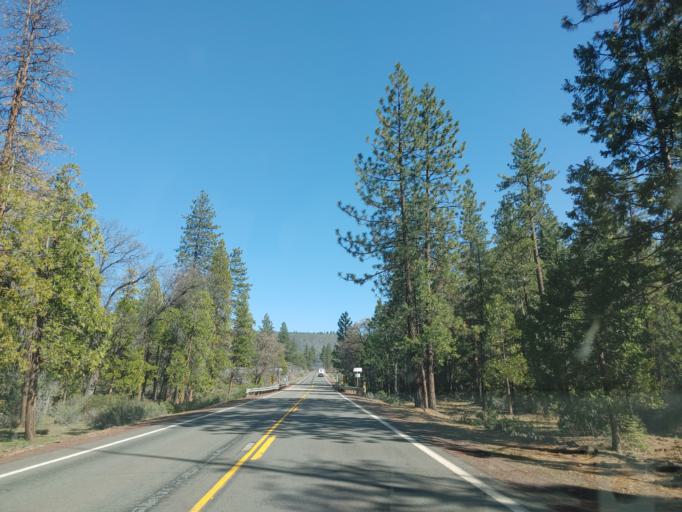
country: US
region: California
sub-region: Shasta County
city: Burney
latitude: 40.7312
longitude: -121.4383
